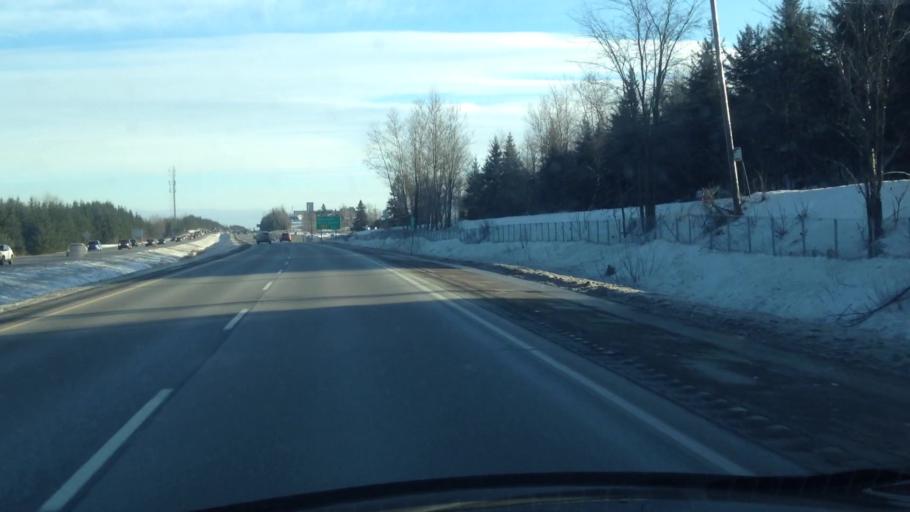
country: CA
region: Quebec
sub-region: Laurentides
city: Saint-Jerome
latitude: 45.8134
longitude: -74.0483
